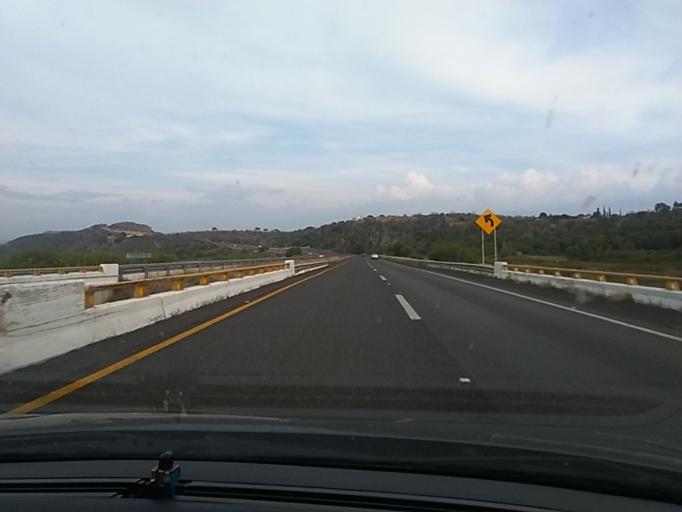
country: MX
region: Michoacan
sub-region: Zinapecuaro
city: Francisco Villa
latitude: 19.8825
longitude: -100.9399
